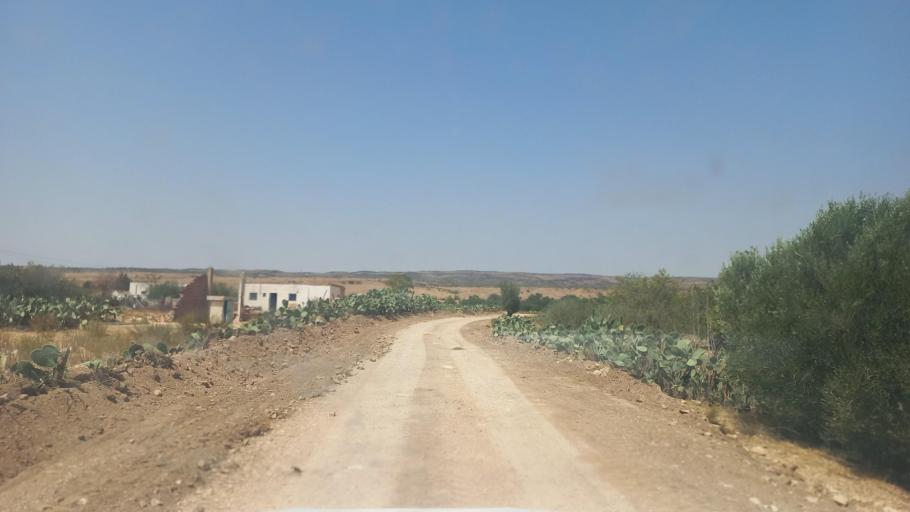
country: TN
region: Al Qasrayn
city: Kasserine
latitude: 35.2937
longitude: 8.9477
